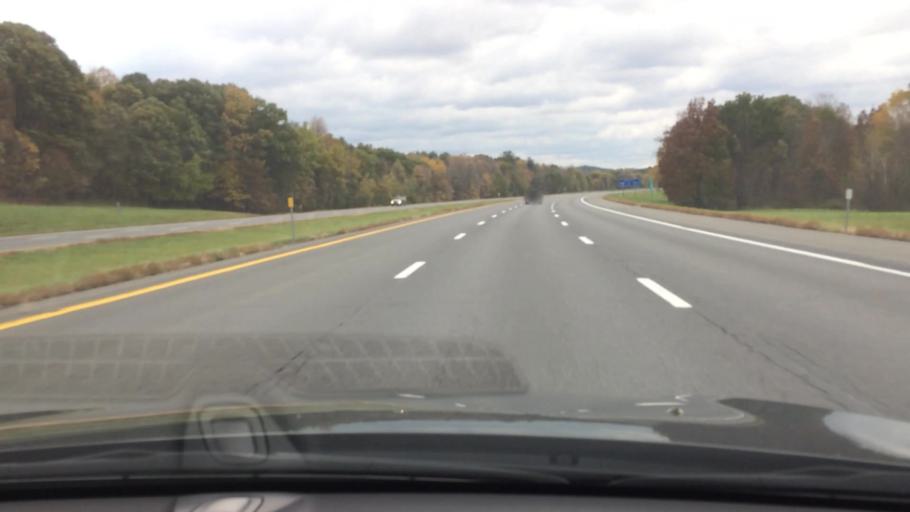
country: US
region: New York
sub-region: Rensselaer County
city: East Greenbush
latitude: 42.5935
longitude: -73.6781
